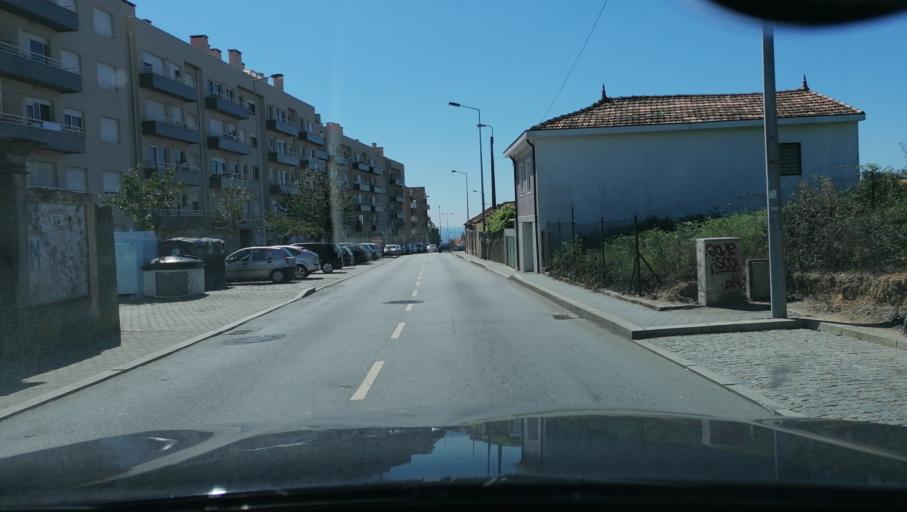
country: PT
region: Porto
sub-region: Vila Nova de Gaia
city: Canidelo
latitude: 41.1309
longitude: -8.6482
